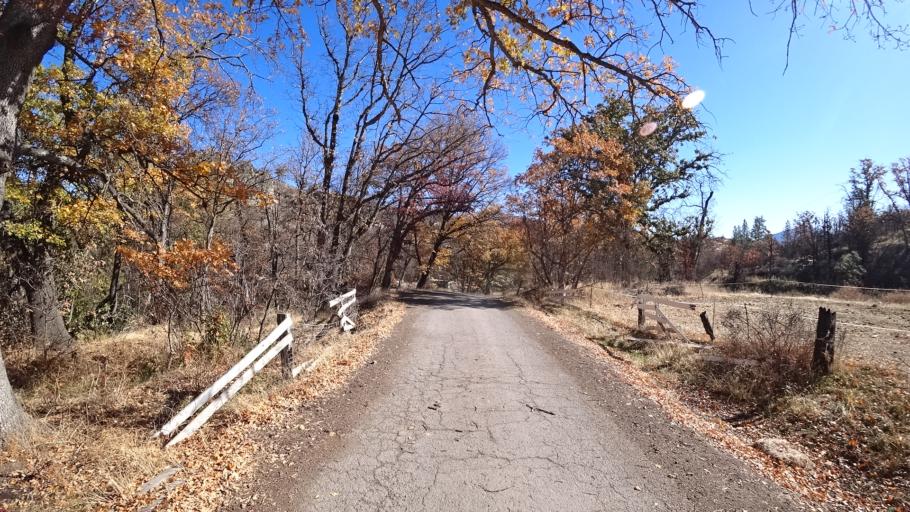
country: US
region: California
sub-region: Siskiyou County
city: Yreka
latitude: 41.9431
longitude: -122.5934
